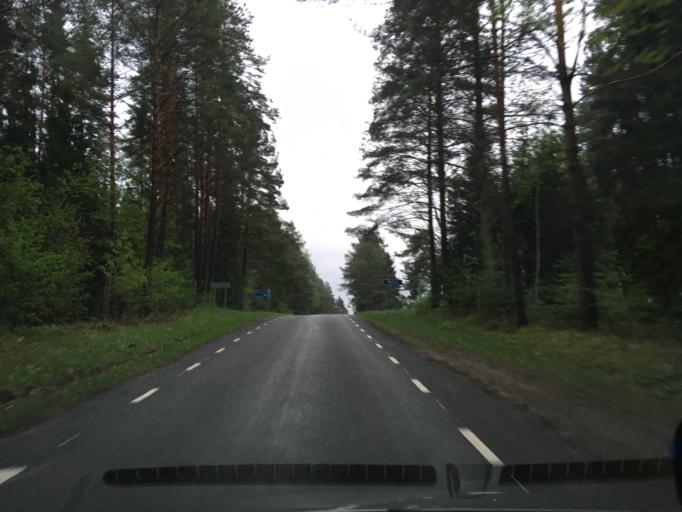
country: EE
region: Harju
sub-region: Keila linn
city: Keila
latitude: 59.1992
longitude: 24.4692
